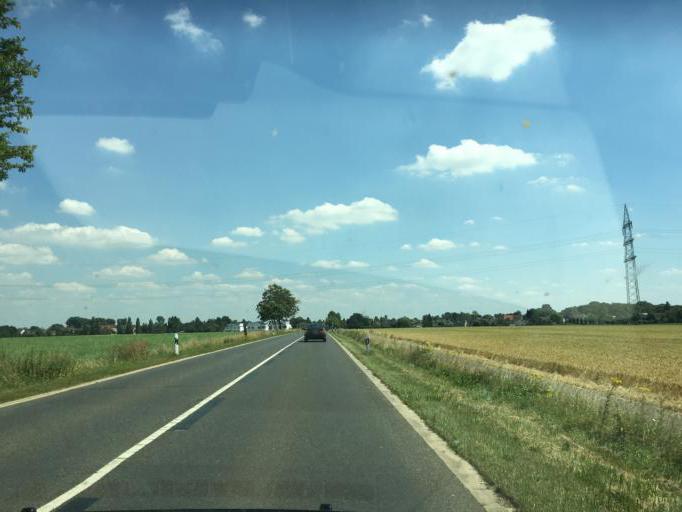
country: DE
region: North Rhine-Westphalia
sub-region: Regierungsbezirk Koln
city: Dueren
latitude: 50.7911
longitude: 6.4290
